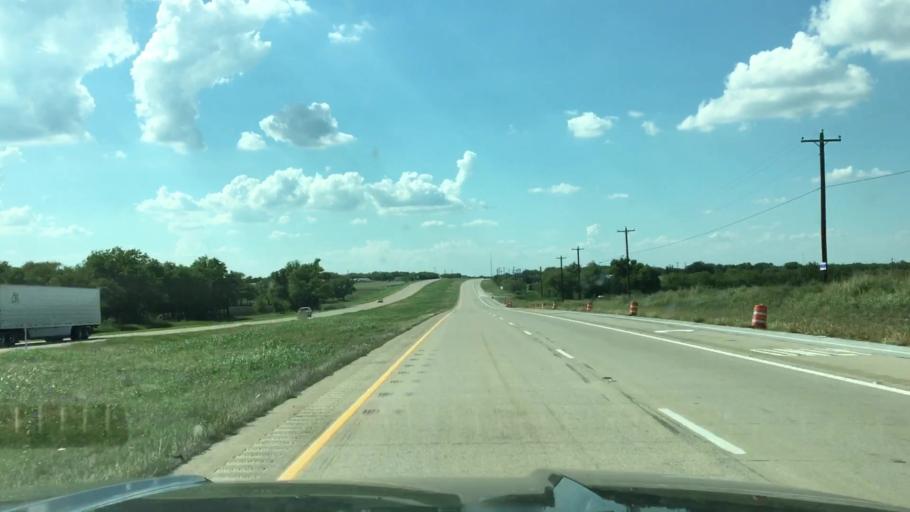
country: US
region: Texas
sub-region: Wise County
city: Rhome
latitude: 33.0389
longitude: -97.4436
